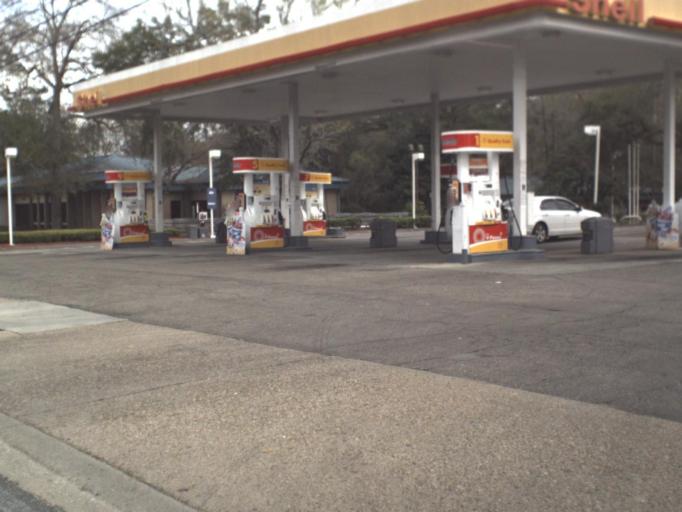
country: US
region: Florida
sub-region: Leon County
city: Tallahassee
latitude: 30.4682
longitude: -84.2674
